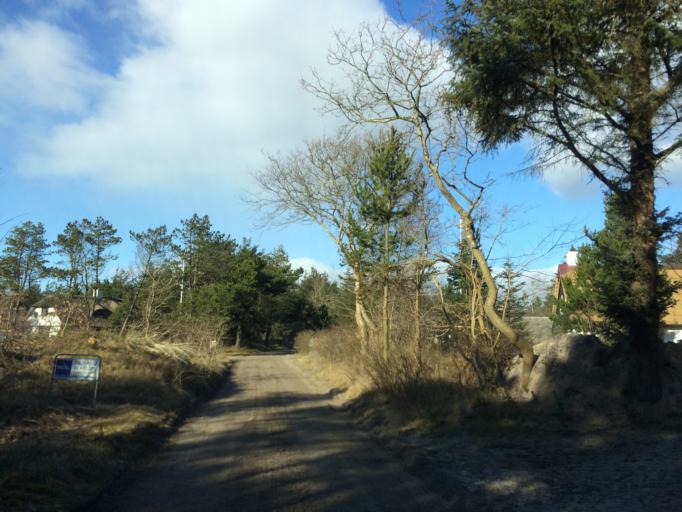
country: DK
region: Central Jutland
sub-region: Holstebro Kommune
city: Ulfborg
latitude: 56.2604
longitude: 8.1437
